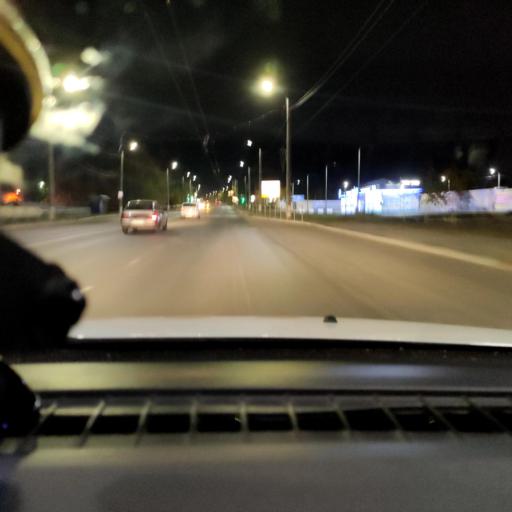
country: RU
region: Samara
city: Novokuybyshevsk
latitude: 53.0965
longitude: 49.9400
